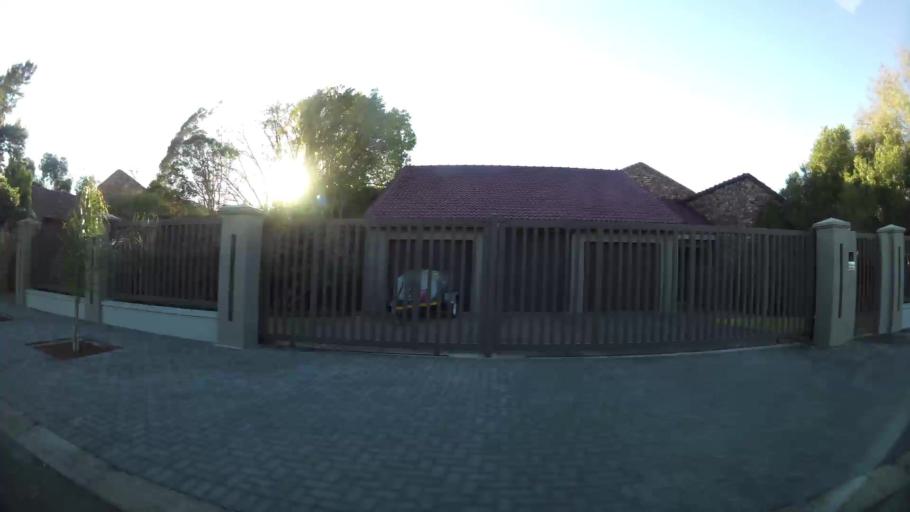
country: ZA
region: Northern Cape
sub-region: Frances Baard District Municipality
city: Kimberley
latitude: -28.7594
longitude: 24.7529
